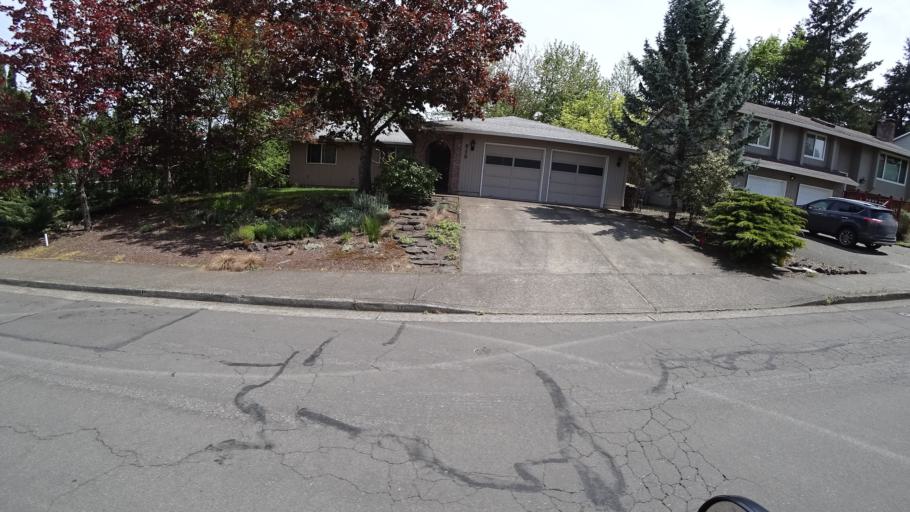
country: US
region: Oregon
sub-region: Washington County
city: Aloha
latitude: 45.4609
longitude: -122.8453
